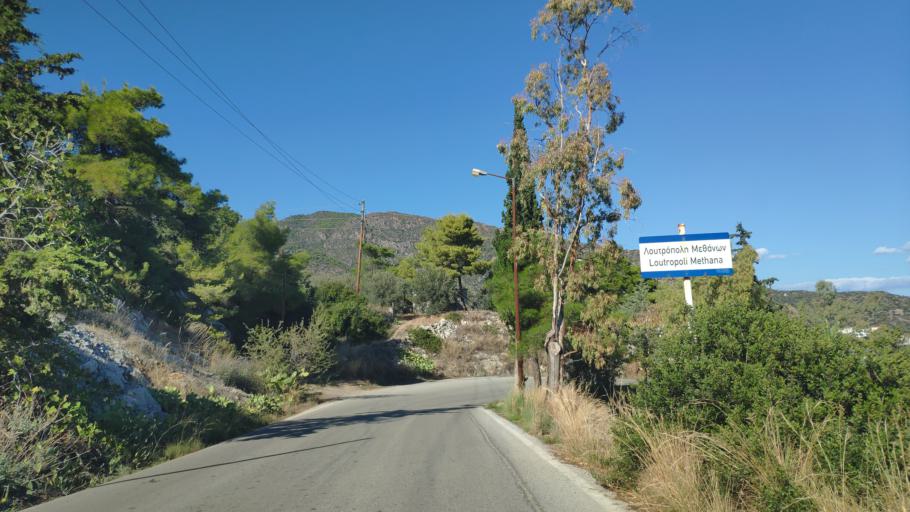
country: GR
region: Attica
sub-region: Nomos Piraios
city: Galatas
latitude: 37.5754
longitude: 23.3874
